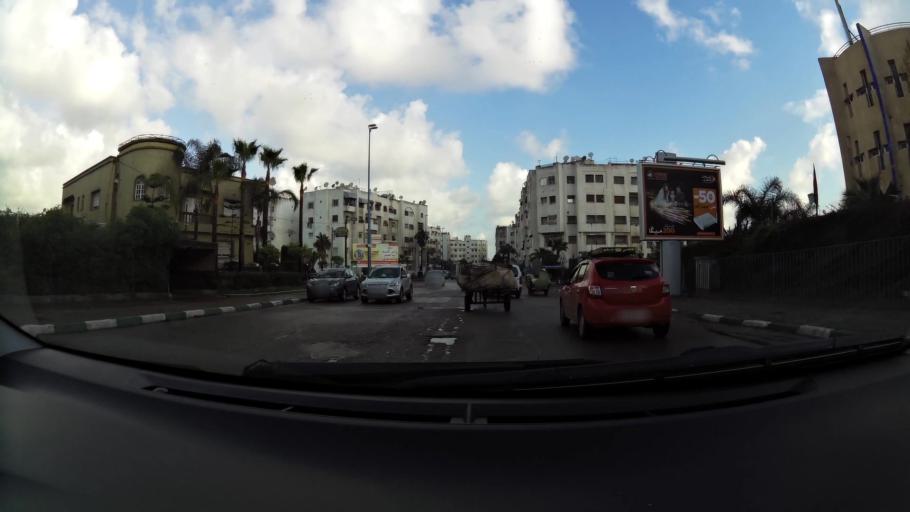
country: MA
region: Grand Casablanca
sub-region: Mediouna
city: Tit Mellil
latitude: 33.5970
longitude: -7.5198
